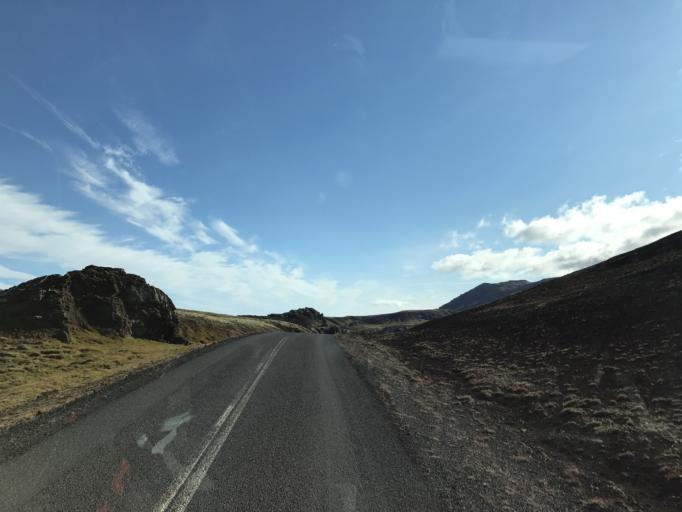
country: IS
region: South
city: Hveragerdi
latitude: 64.1229
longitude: -21.3046
